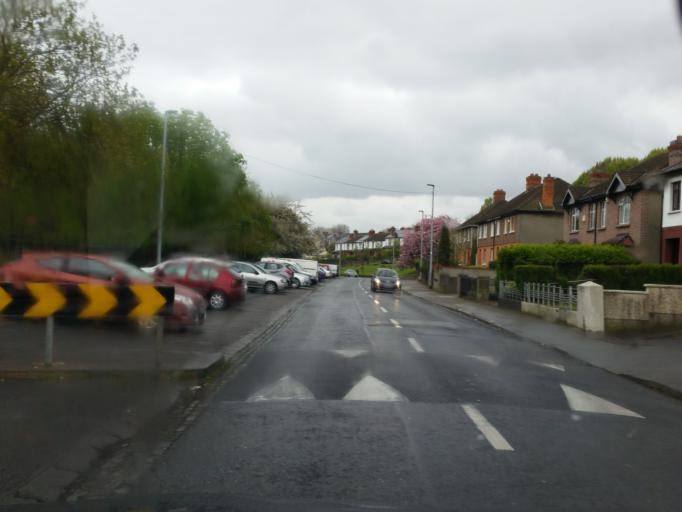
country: IE
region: Leinster
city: Drumcondra
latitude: 53.3699
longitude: -6.2633
